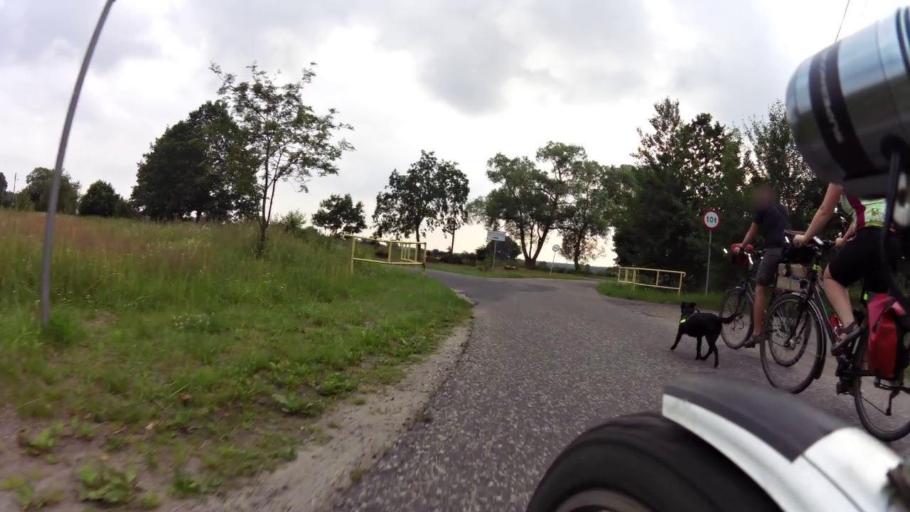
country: PL
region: West Pomeranian Voivodeship
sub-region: Powiat policki
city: Police
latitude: 53.6299
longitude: 14.4675
